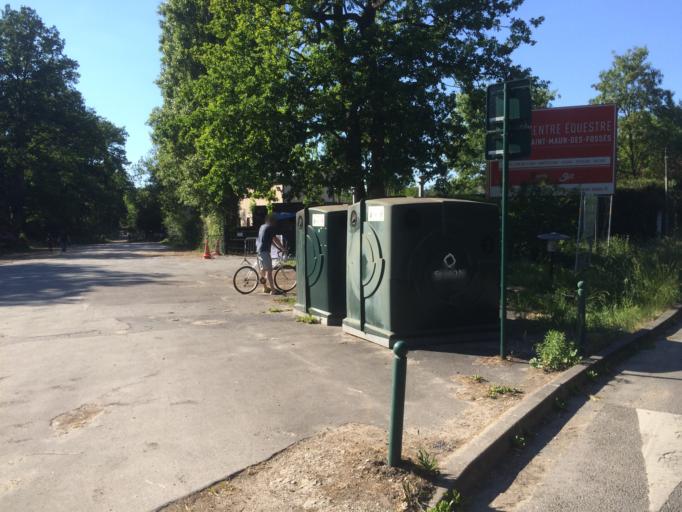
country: FR
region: Ile-de-France
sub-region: Departement du Val-de-Marne
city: Santeny
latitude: 48.7467
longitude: 2.5570
